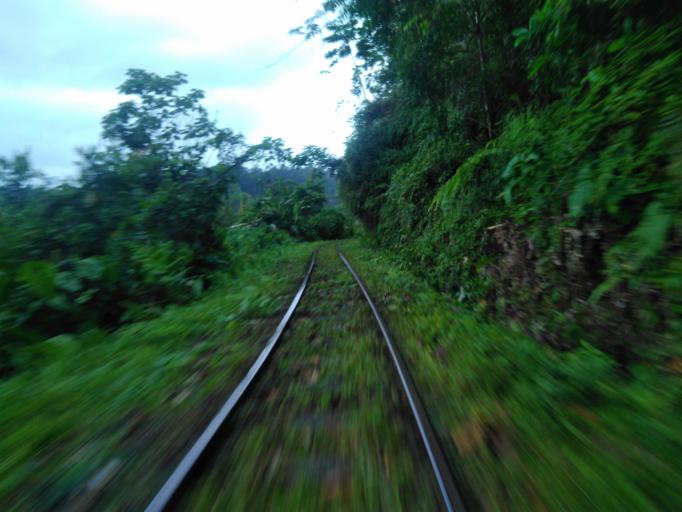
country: CO
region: Valle del Cauca
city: Buenaventura
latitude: 3.8418
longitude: -76.8702
